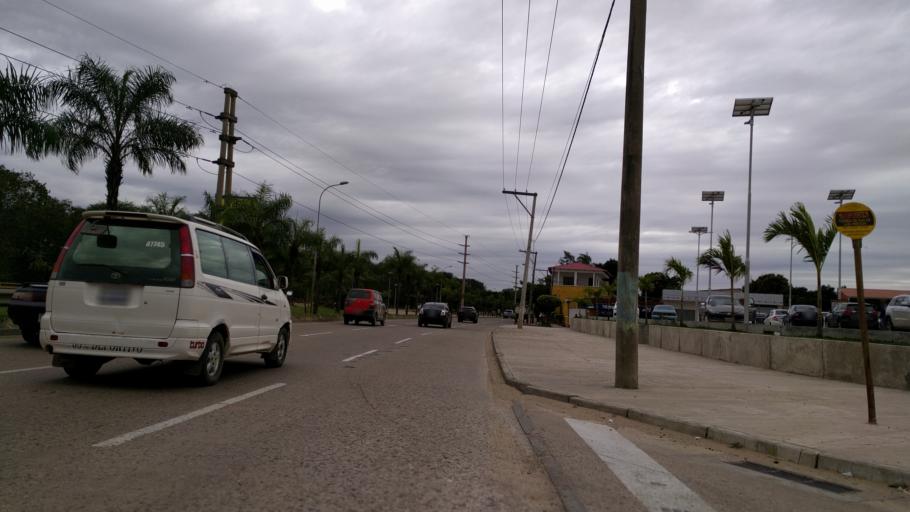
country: BO
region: Santa Cruz
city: Santa Cruz de la Sierra
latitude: -17.7767
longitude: -63.2158
